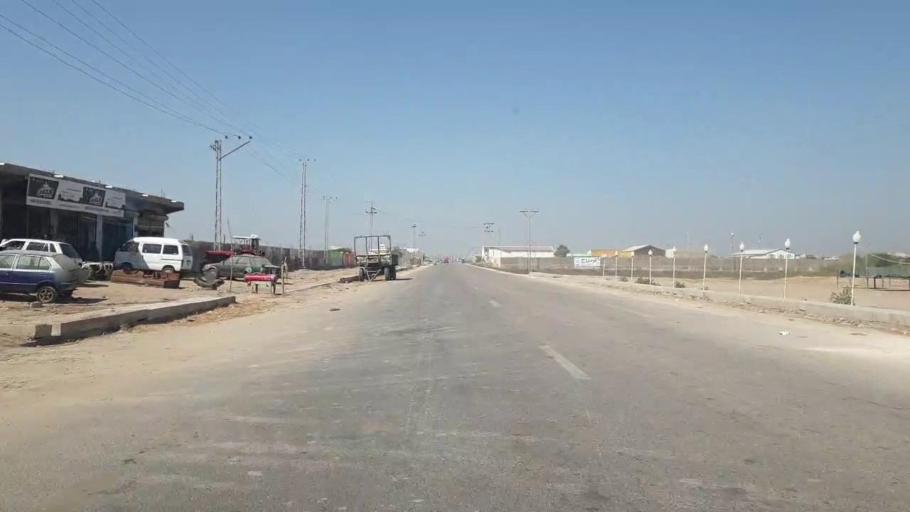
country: PK
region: Sindh
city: Talhar
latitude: 24.8750
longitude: 68.8154
